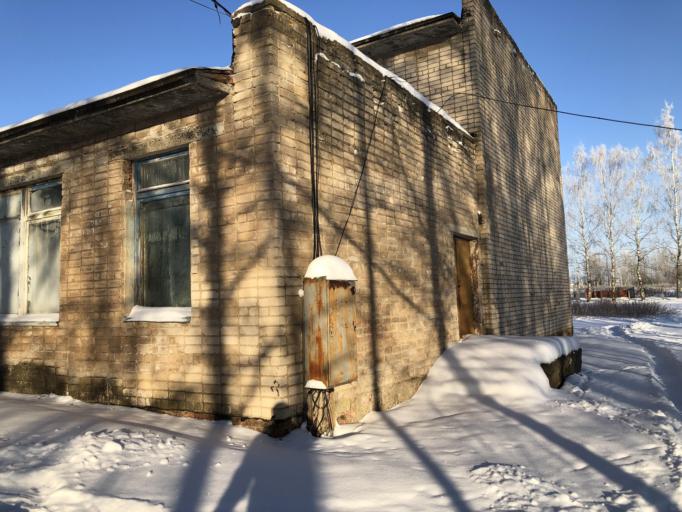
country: RU
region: Smolensk
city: Safonovo
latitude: 55.0864
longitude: 33.0702
